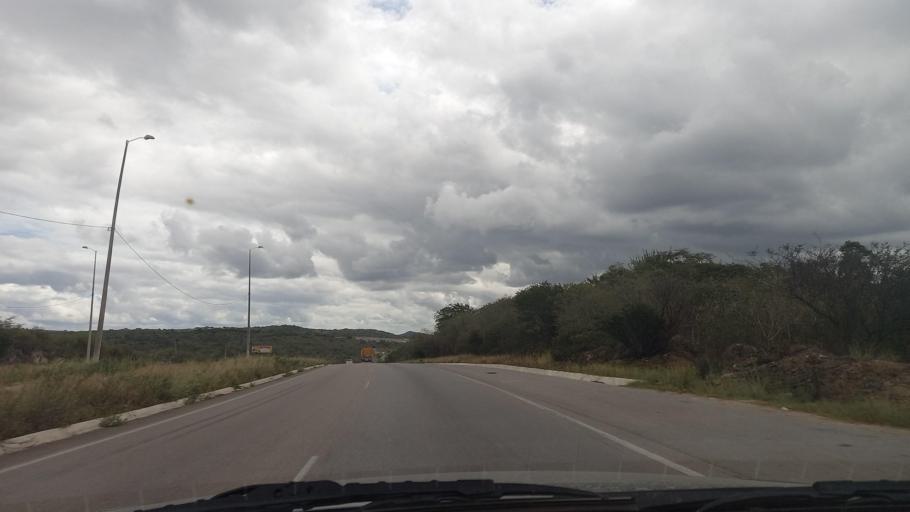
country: BR
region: Pernambuco
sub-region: Caruaru
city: Caruaru
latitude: -8.3213
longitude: -36.0859
